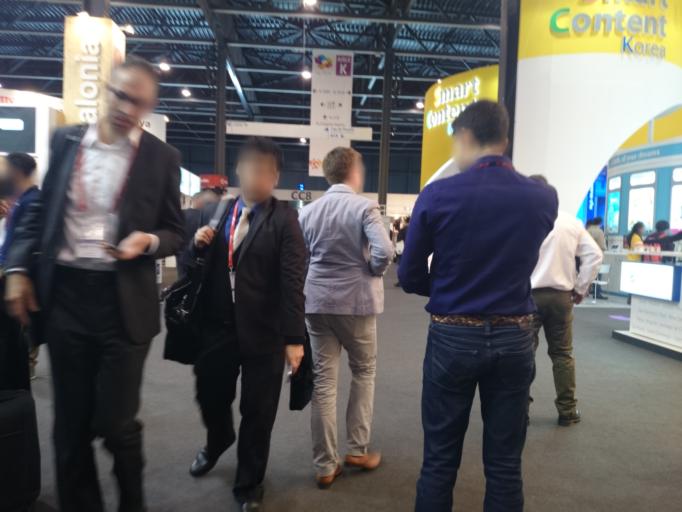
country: ES
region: Catalonia
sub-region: Provincia de Barcelona
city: Sants-Montjuic
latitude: 41.3557
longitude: 2.1371
